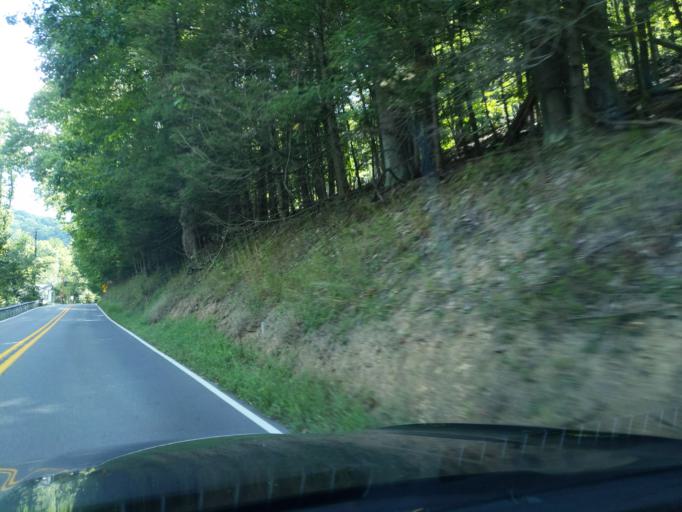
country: US
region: Pennsylvania
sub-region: Blair County
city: Greenwood
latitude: 40.5335
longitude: -78.2941
